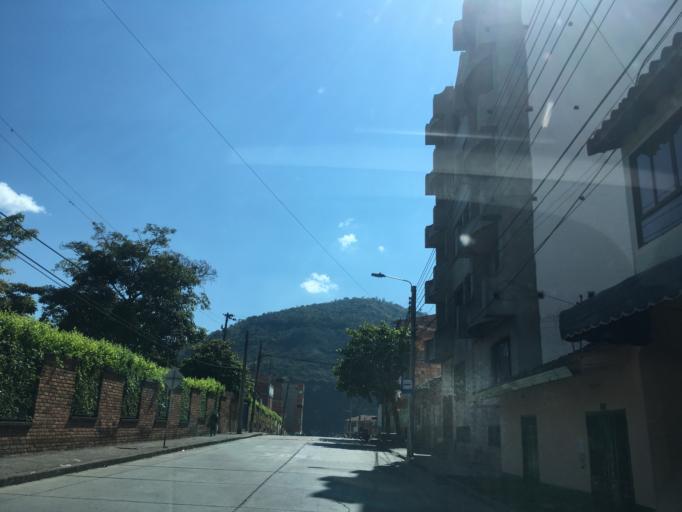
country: CO
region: Santander
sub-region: San Gil
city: San Gil
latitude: 6.5560
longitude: -73.1281
